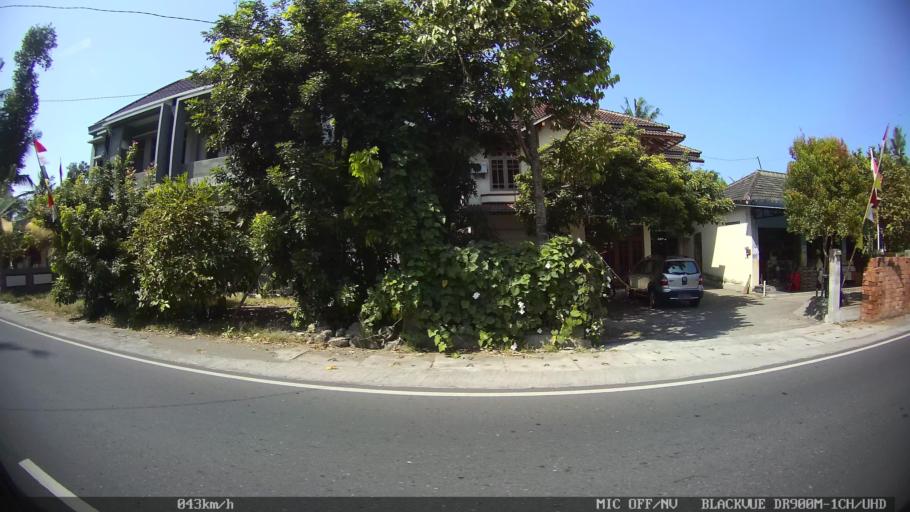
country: ID
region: Daerah Istimewa Yogyakarta
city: Srandakan
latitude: -7.9299
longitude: 110.2036
